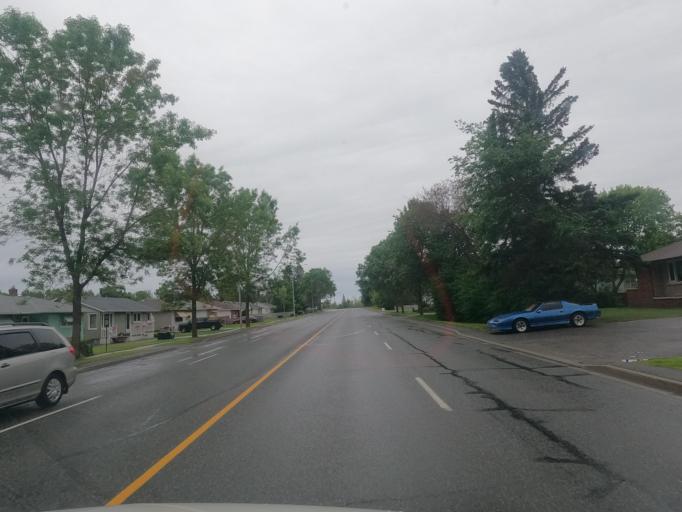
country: CA
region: Ontario
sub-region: Thunder Bay District
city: Thunder Bay
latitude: 48.4604
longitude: -89.1823
